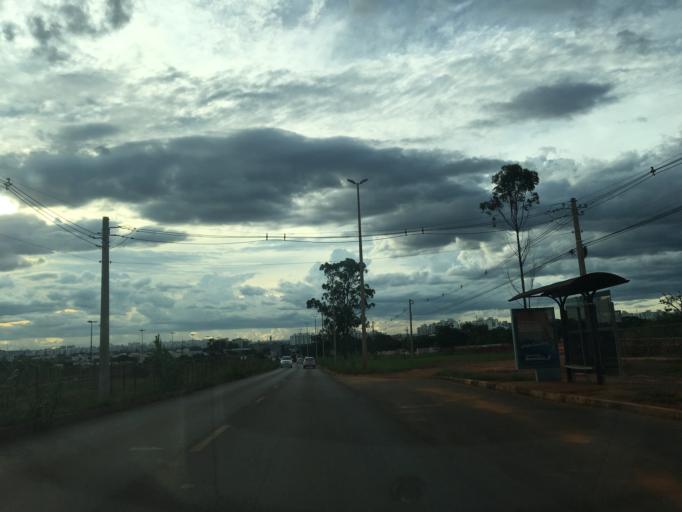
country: BR
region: Federal District
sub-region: Brasilia
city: Brasilia
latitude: -15.8326
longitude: -47.9445
